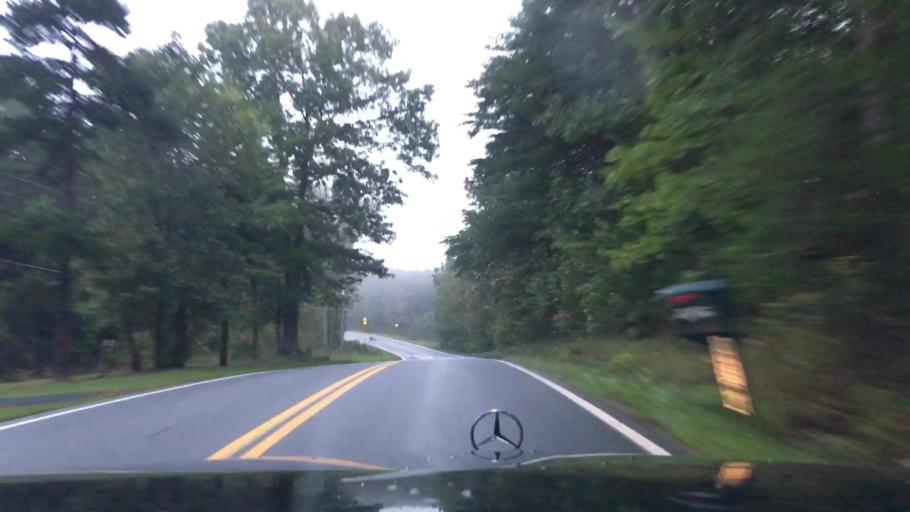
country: US
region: Virginia
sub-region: Campbell County
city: Timberlake
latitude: 37.2517
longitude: -79.2794
